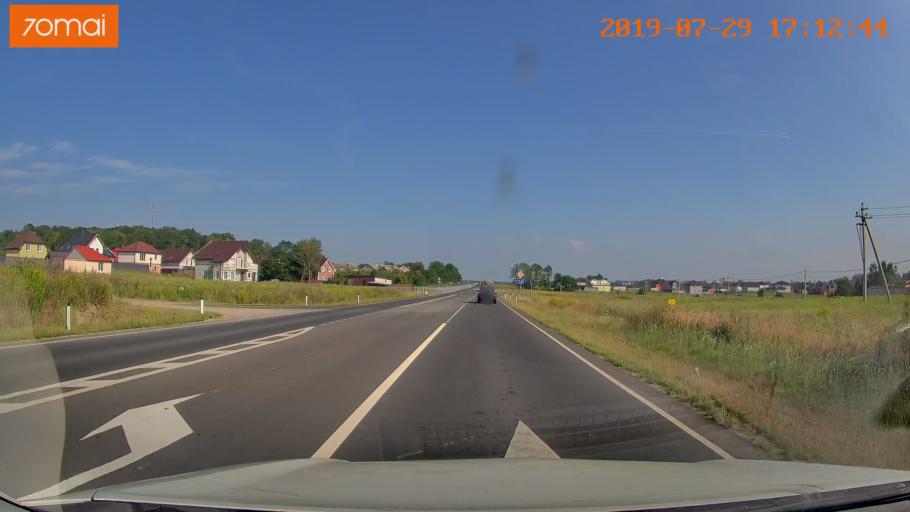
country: RU
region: Kaliningrad
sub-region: Gorod Kaliningrad
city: Kaliningrad
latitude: 54.7867
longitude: 20.4019
